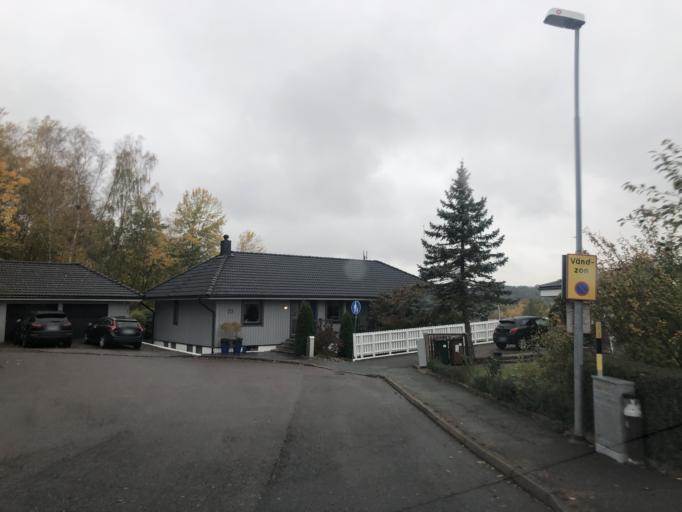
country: SE
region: Vaestra Goetaland
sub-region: Goteborg
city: Majorna
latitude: 57.6323
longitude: 11.9185
